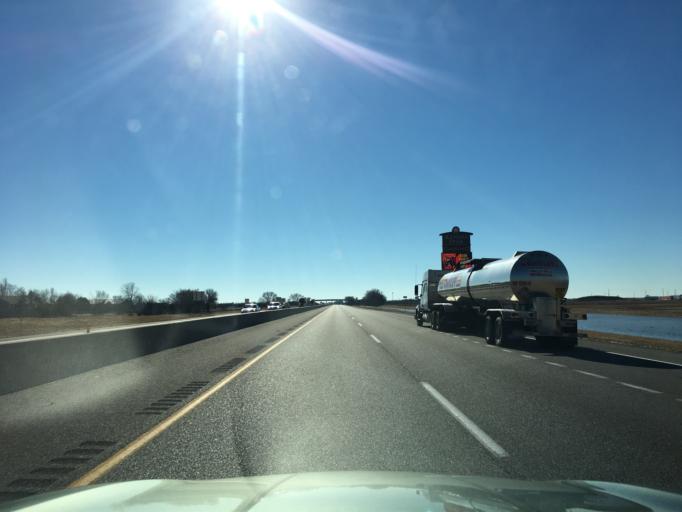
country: US
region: Kansas
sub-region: Sumner County
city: Mulvane
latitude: 37.4716
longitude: -97.3229
